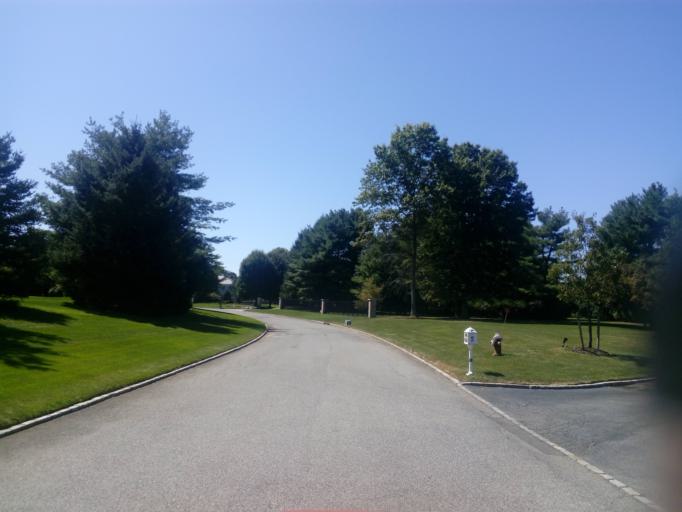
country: US
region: New York
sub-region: Nassau County
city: Upper Brookville
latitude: 40.8385
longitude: -73.5797
